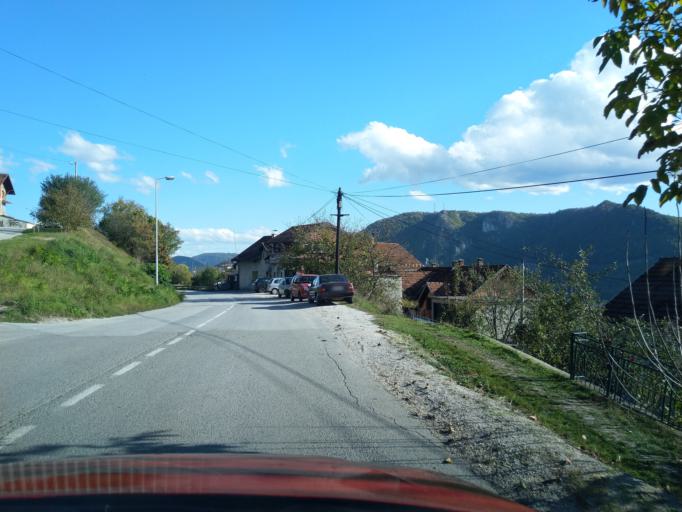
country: RS
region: Central Serbia
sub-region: Zlatiborski Okrug
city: Uzice
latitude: 43.8631
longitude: 19.8148
